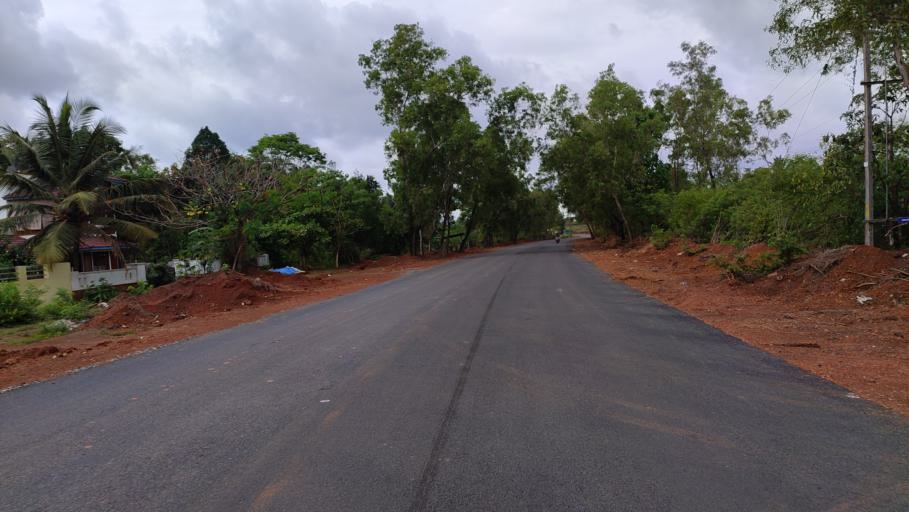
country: IN
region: Kerala
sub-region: Kasaragod District
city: Kasaragod
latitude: 12.5526
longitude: 75.0712
